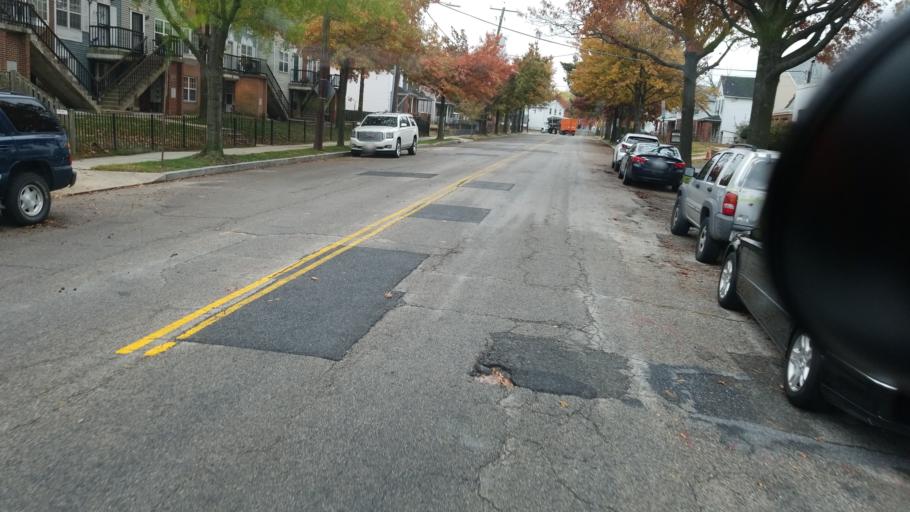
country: US
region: Maryland
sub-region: Prince George's County
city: Fairmount Heights
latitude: 38.9072
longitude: -76.9353
